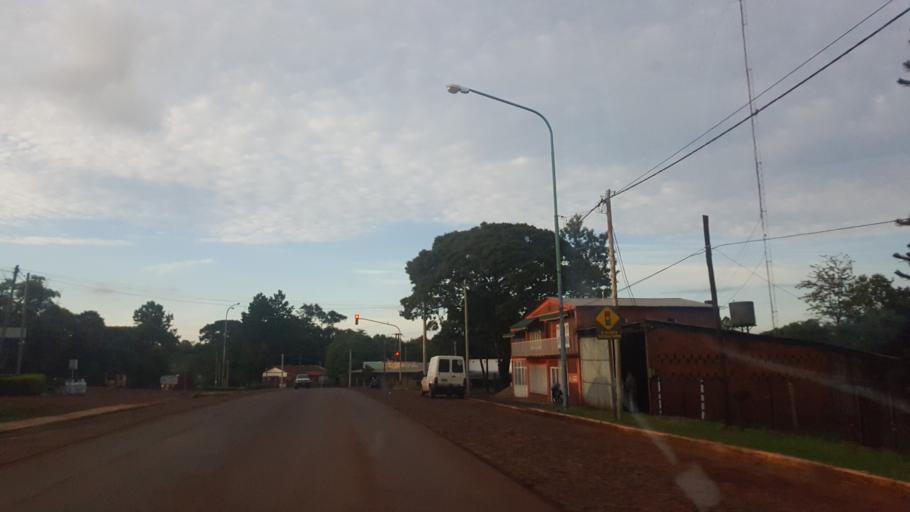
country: AR
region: Misiones
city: Dos de Mayo
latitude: -27.0192
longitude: -54.6872
